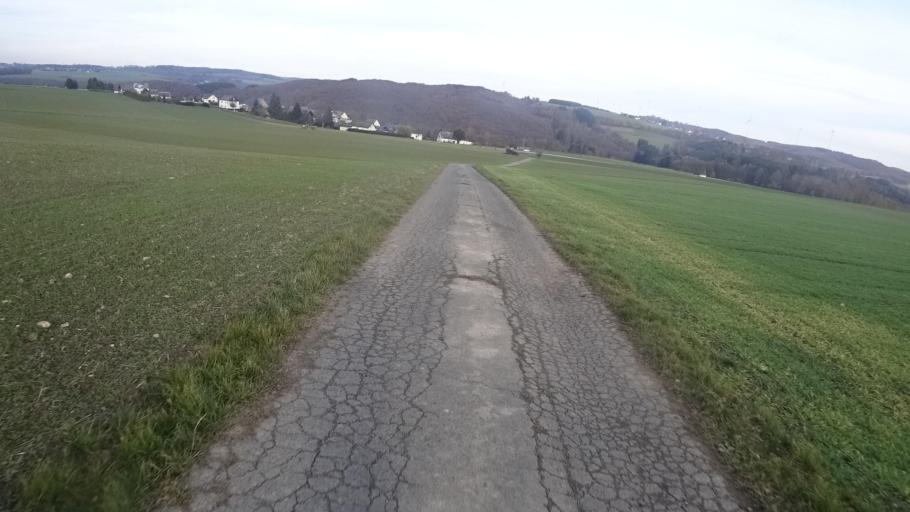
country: DE
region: Rheinland-Pfalz
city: Muhlpfad
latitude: 50.1176
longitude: 7.5524
